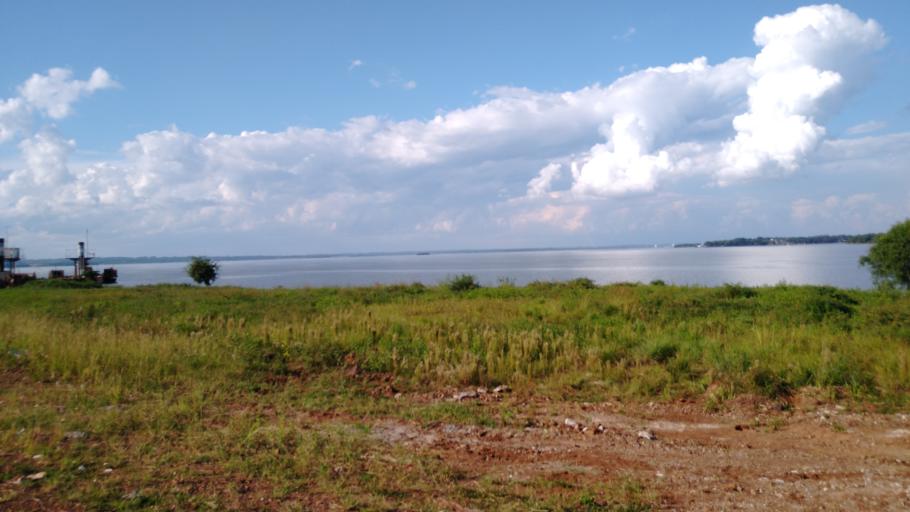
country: PY
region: Itapua
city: San Juan del Parana
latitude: -27.3702
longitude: -55.9846
